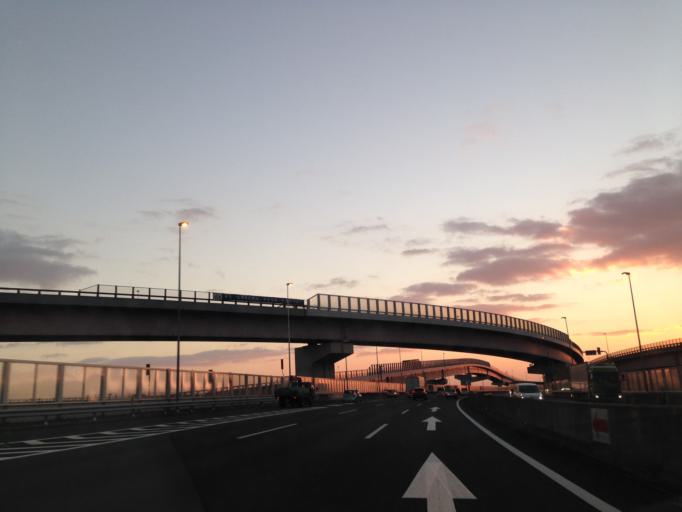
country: JP
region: Aichi
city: Obu
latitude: 35.0485
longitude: 136.9440
